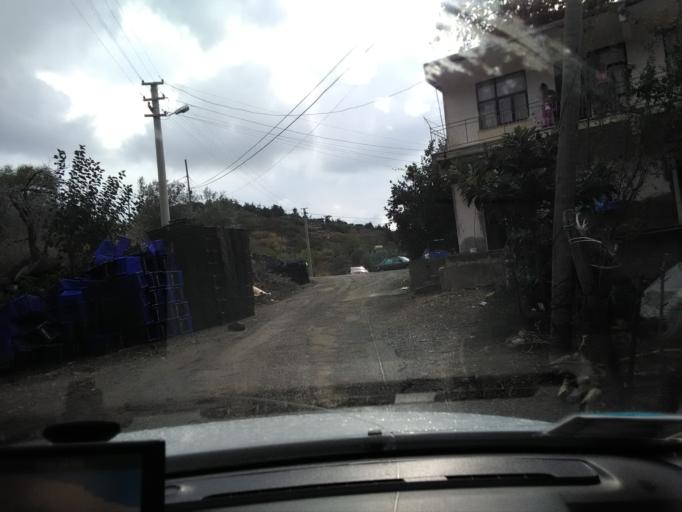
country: TR
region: Antalya
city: Gazipasa
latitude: 36.1563
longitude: 32.4254
